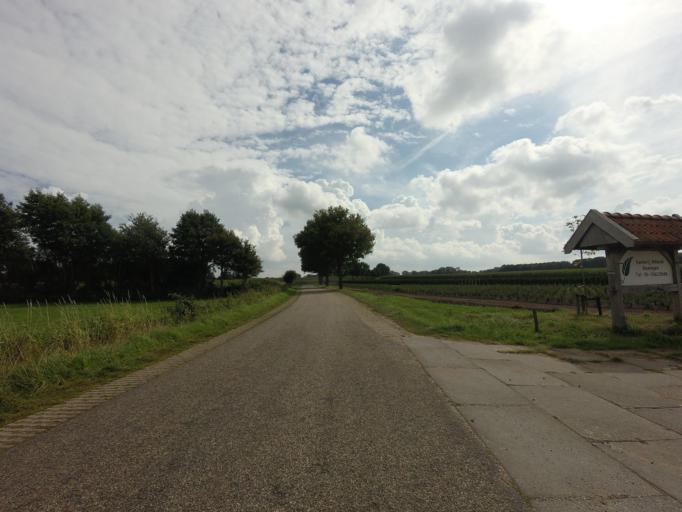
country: DE
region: Lower Saxony
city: Nordhorn
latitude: 52.3629
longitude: 7.0090
